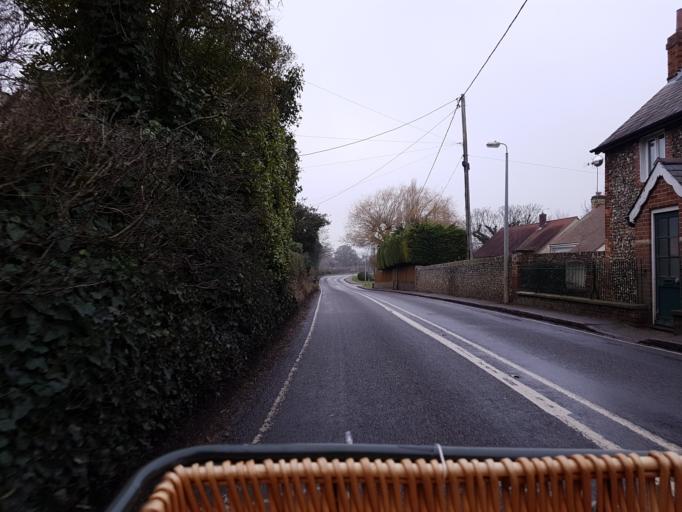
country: GB
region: England
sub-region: Cambridgeshire
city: Duxford
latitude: 52.0656
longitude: 0.1944
